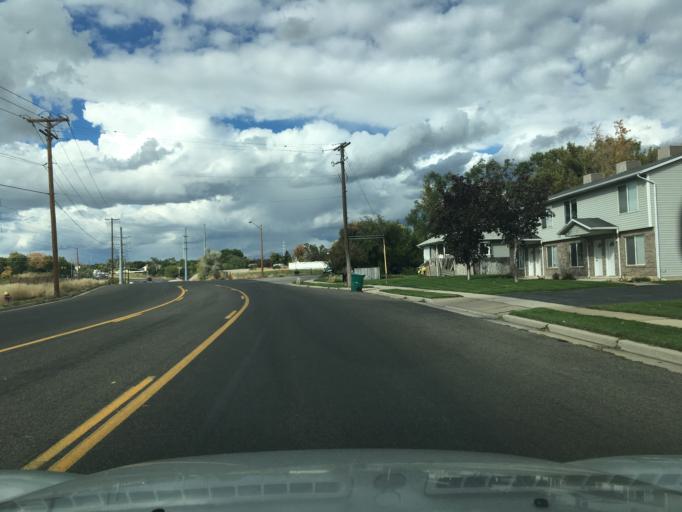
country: US
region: Utah
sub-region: Davis County
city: Layton
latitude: 41.0714
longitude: -111.9574
